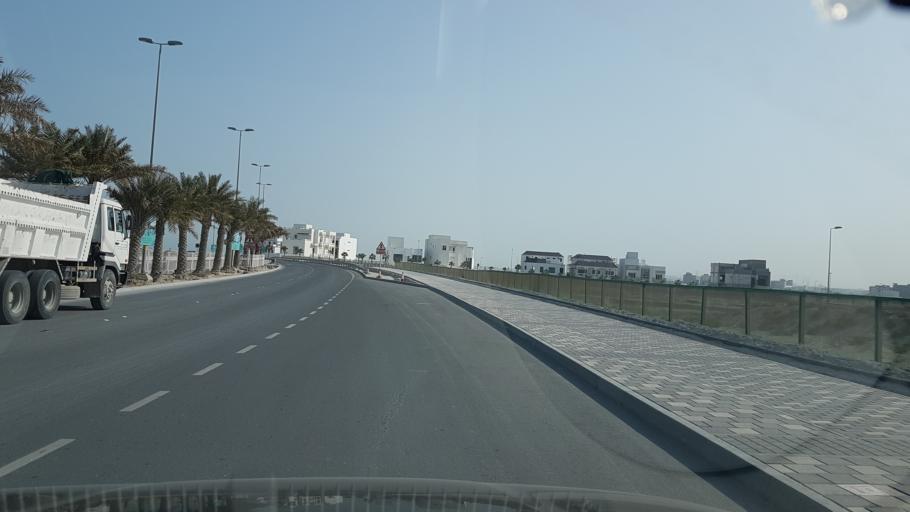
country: BH
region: Muharraq
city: Al Hadd
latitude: 26.2706
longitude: 50.6697
